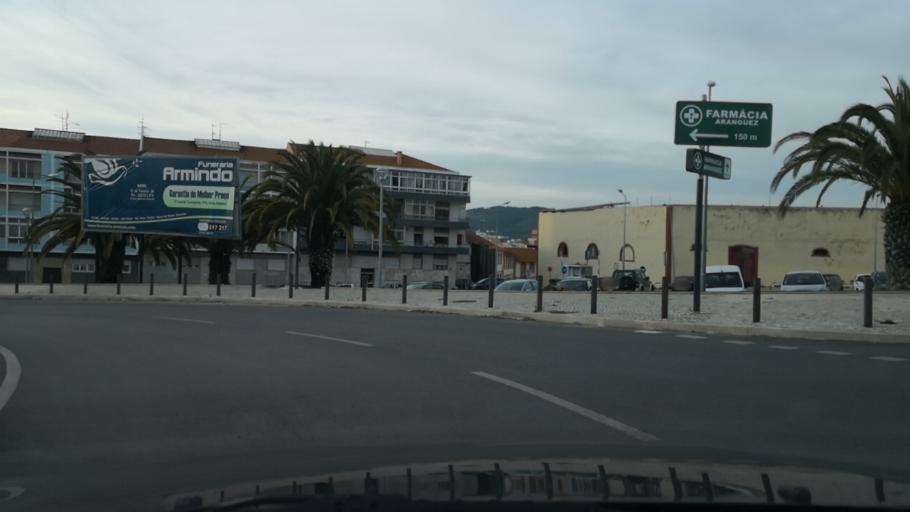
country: PT
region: Setubal
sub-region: Setubal
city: Setubal
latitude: 38.5290
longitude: -8.8820
